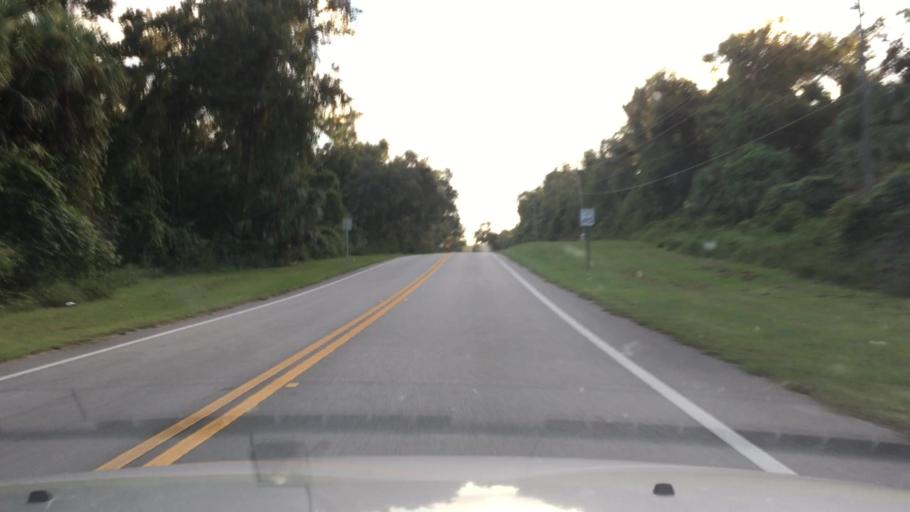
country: US
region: Florida
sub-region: Volusia County
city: Ormond Beach
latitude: 29.3013
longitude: -81.1044
